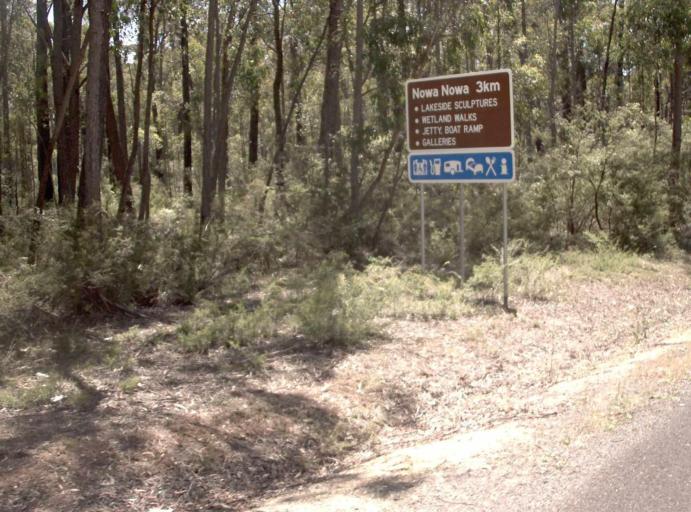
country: AU
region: Victoria
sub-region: East Gippsland
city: Lakes Entrance
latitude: -37.7505
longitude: 148.0687
